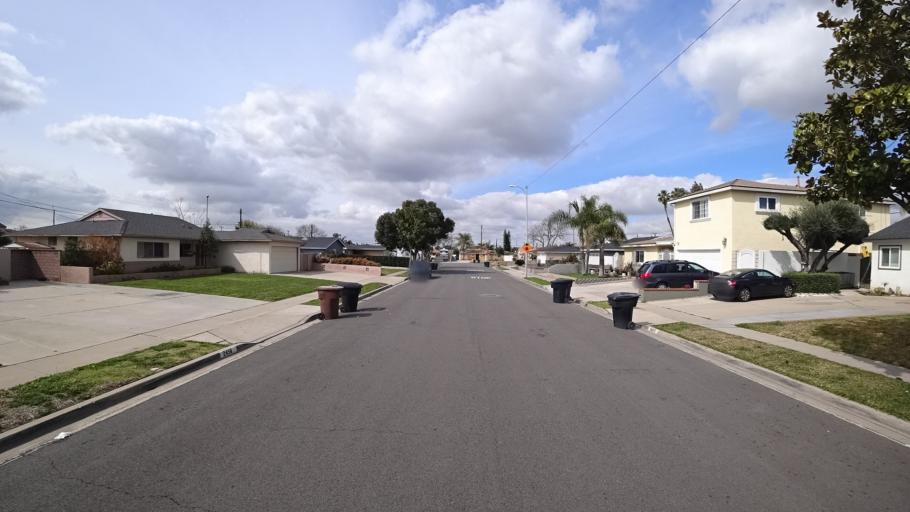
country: US
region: California
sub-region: Orange County
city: Buena Park
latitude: 33.8439
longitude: -117.9706
